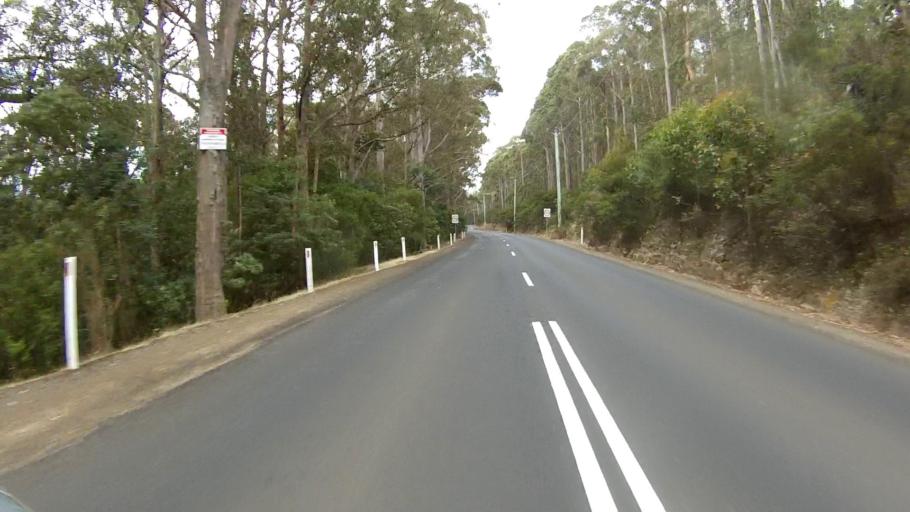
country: AU
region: Tasmania
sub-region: Hobart
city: Dynnyrne
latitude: -42.9118
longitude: 147.2697
